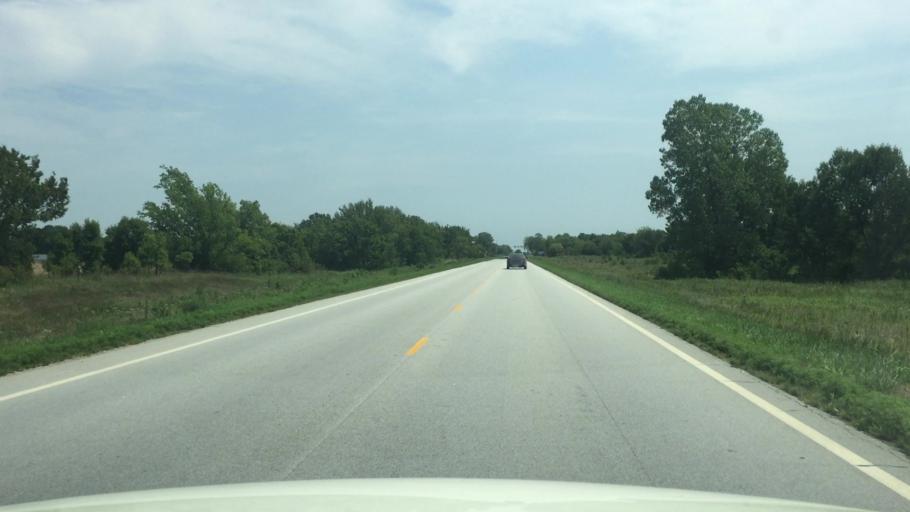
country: US
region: Kansas
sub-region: Cherokee County
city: Columbus
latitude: 37.1796
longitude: -94.9540
